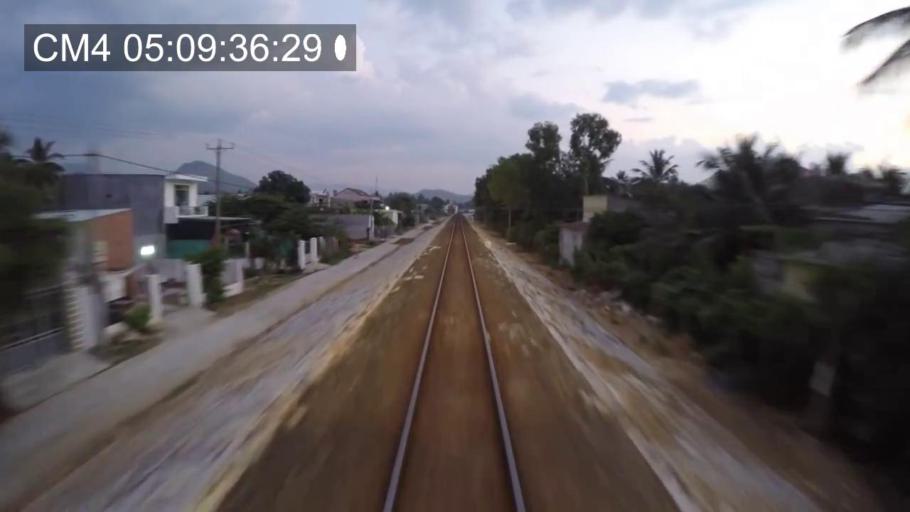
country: VN
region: Khanh Hoa
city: Nha Trang
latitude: 12.3021
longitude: 109.1857
